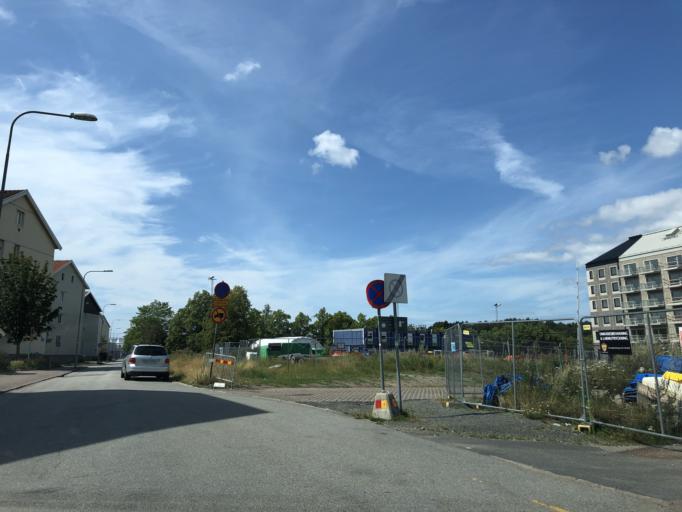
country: SE
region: Vaestra Goetaland
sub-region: Goteborg
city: Majorna
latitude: 57.7172
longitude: 11.9286
